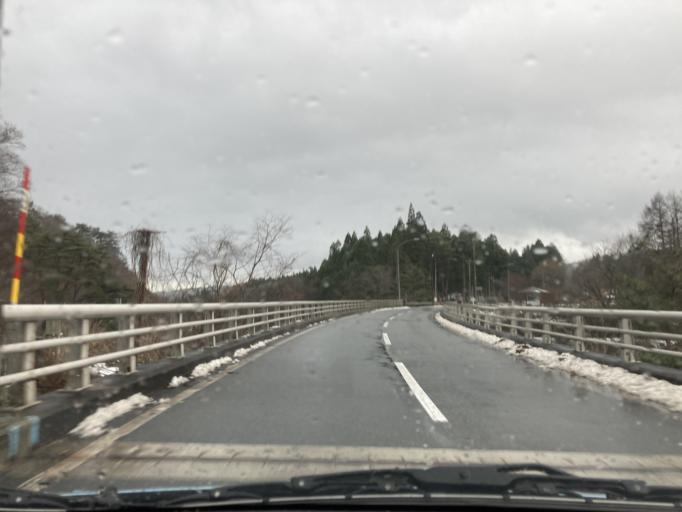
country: JP
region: Iwate
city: Ichinoseki
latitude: 38.9871
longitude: 140.9118
